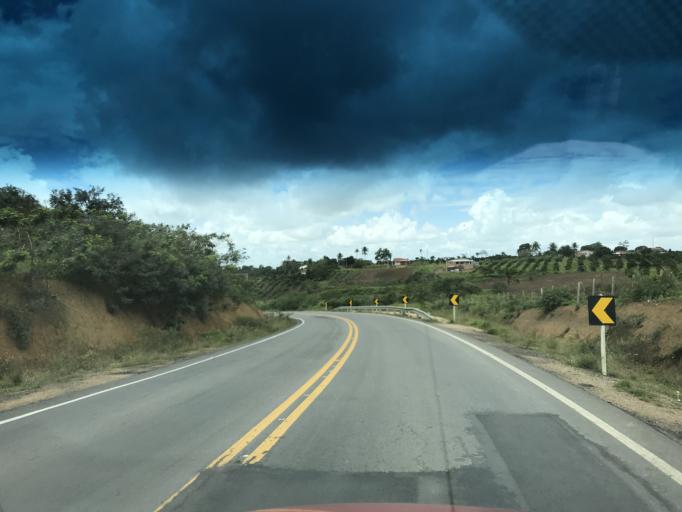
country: BR
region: Bahia
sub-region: Conceicao Do Almeida
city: Conceicao do Almeida
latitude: -12.6982
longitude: -39.2414
